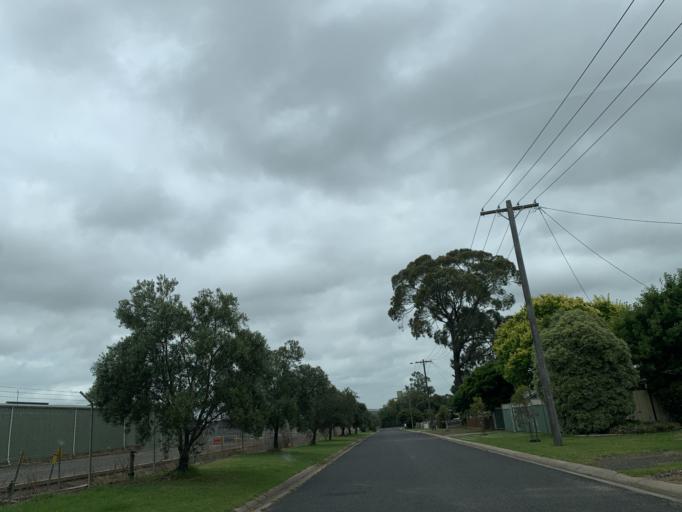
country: AU
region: Victoria
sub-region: Wellington
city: Heyfield
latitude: -37.9790
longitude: 146.7952
